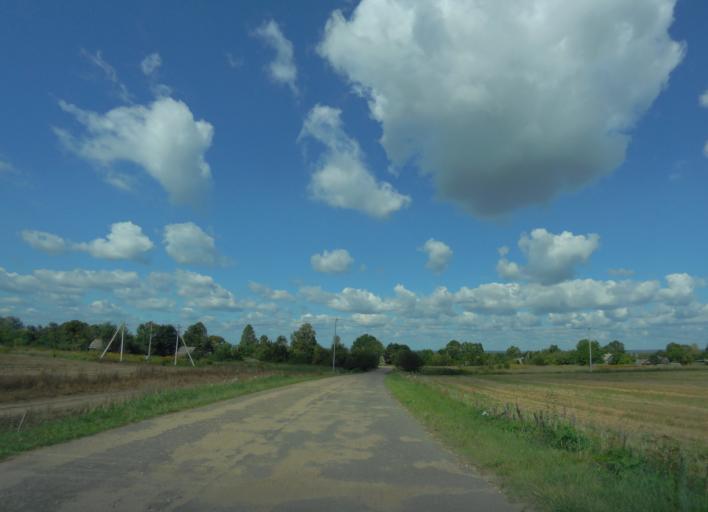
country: BY
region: Minsk
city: Zyembin
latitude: 54.4080
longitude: 28.3892
